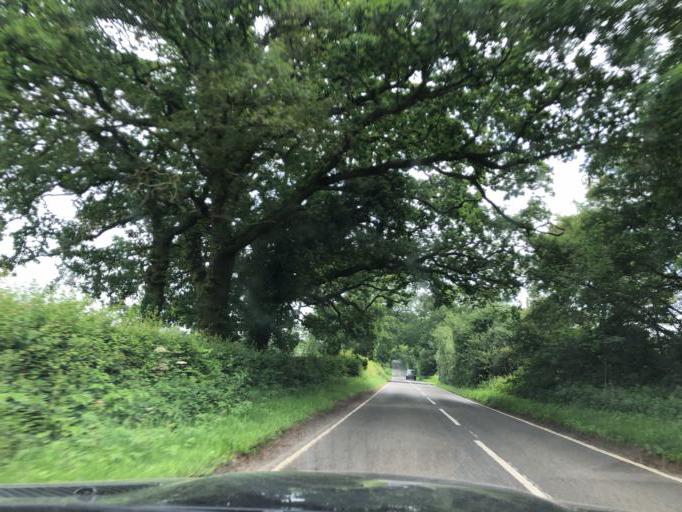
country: GB
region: England
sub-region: Warwickshire
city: Kenilworth
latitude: 52.3257
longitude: -1.6063
